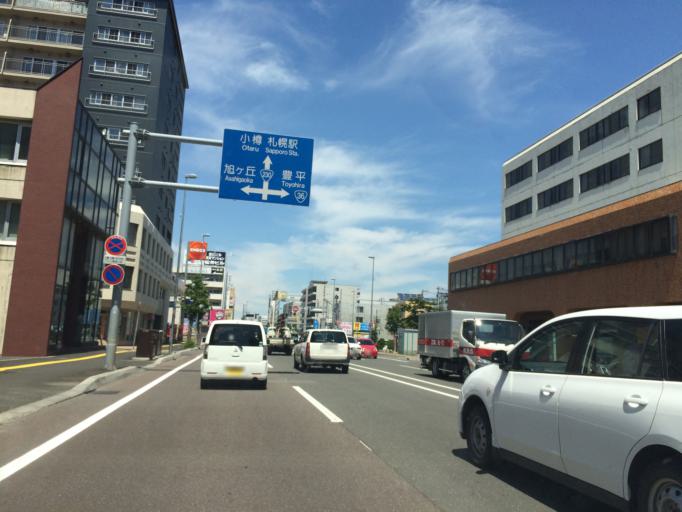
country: JP
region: Hokkaido
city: Sapporo
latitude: 43.0473
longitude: 141.3427
